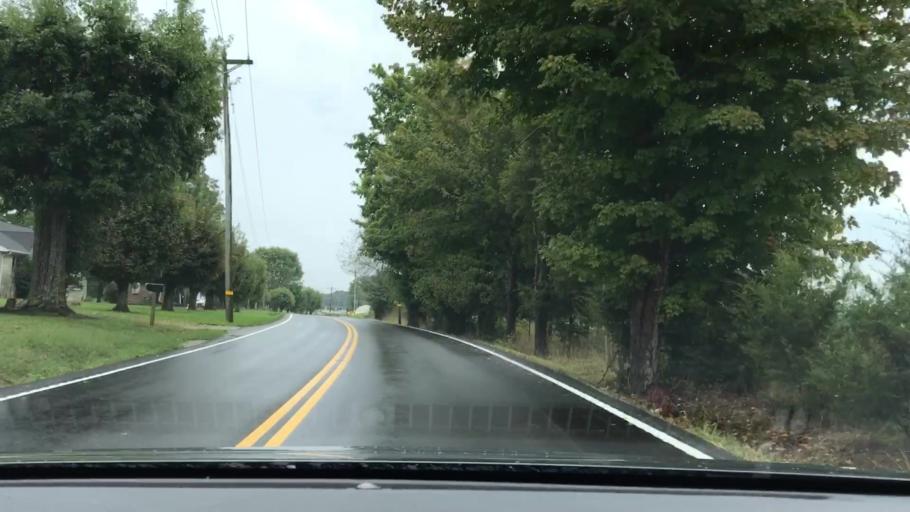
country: US
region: Tennessee
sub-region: Macon County
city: Red Boiling Springs
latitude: 36.5003
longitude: -85.8670
